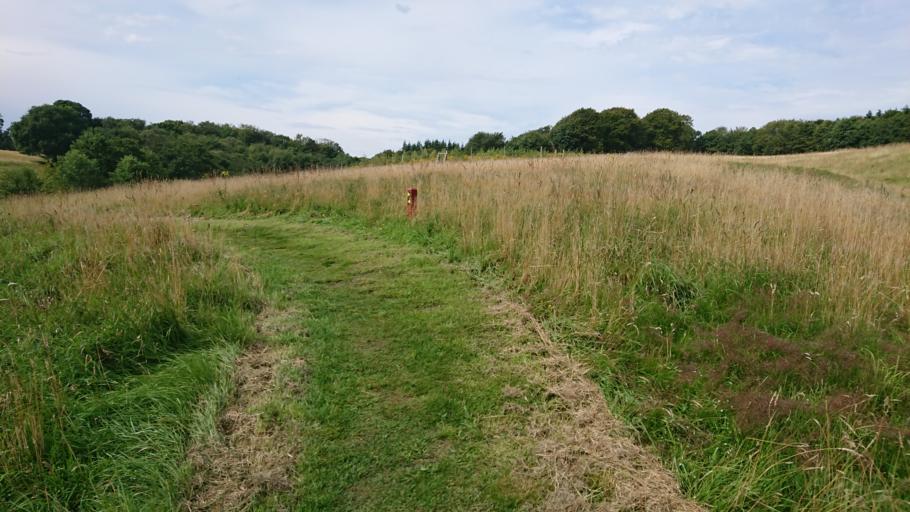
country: DK
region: North Denmark
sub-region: Hjorring Kommune
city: Sindal
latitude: 57.4792
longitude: 10.1810
